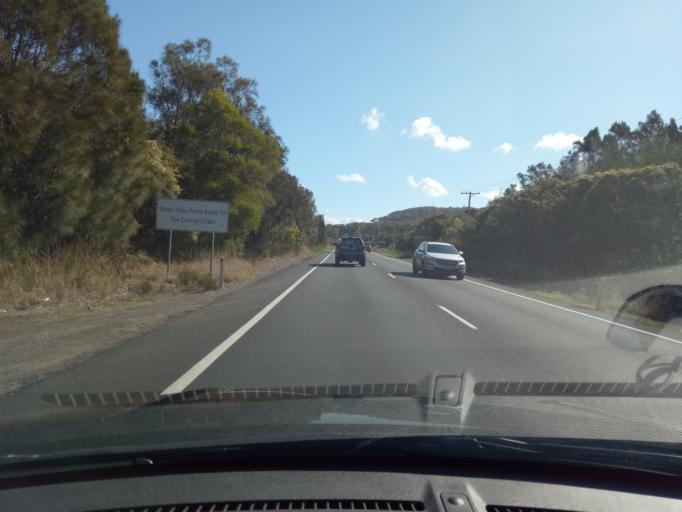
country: AU
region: New South Wales
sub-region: Gosford Shire
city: Forresters Beach
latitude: -33.4112
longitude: 151.4576
